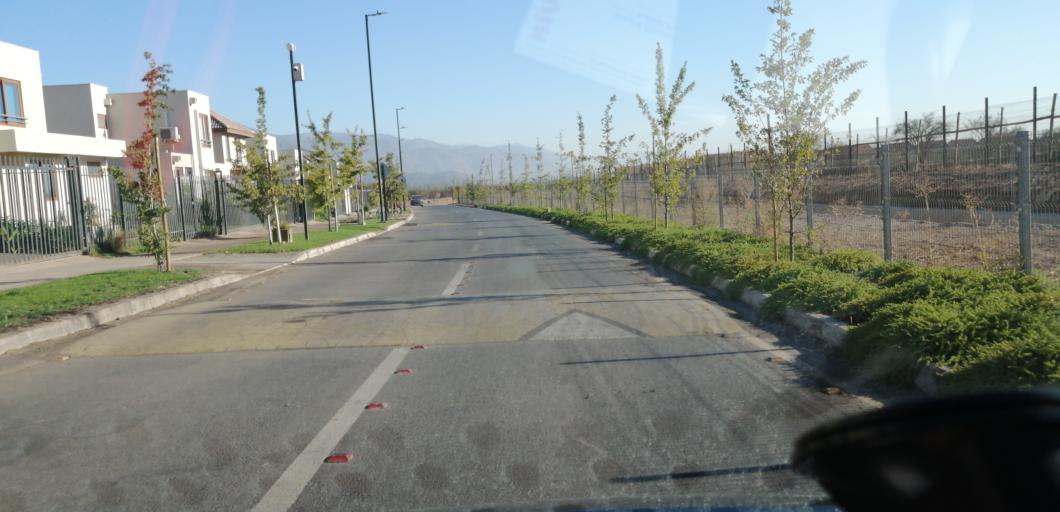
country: CL
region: Santiago Metropolitan
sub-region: Provincia de Santiago
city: Lo Prado
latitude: -33.4681
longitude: -70.8598
